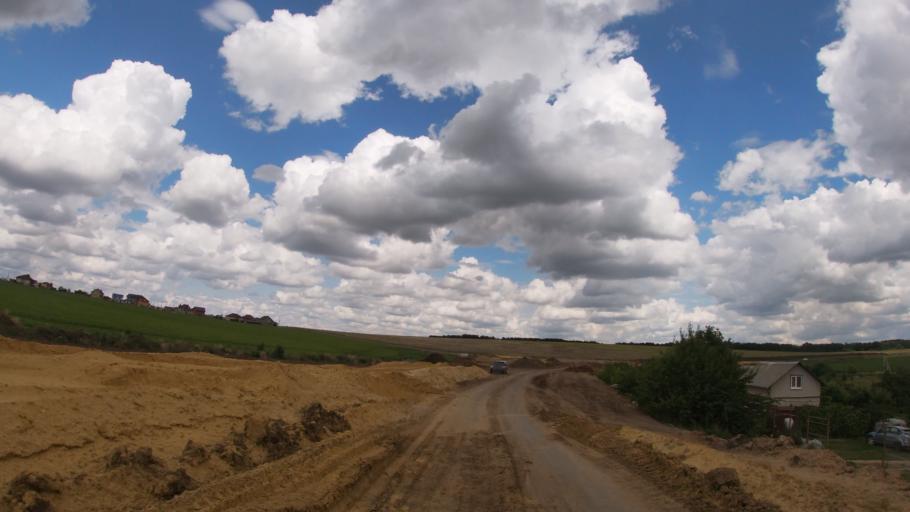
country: RU
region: Belgorod
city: Mayskiy
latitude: 50.5167
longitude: 36.4915
